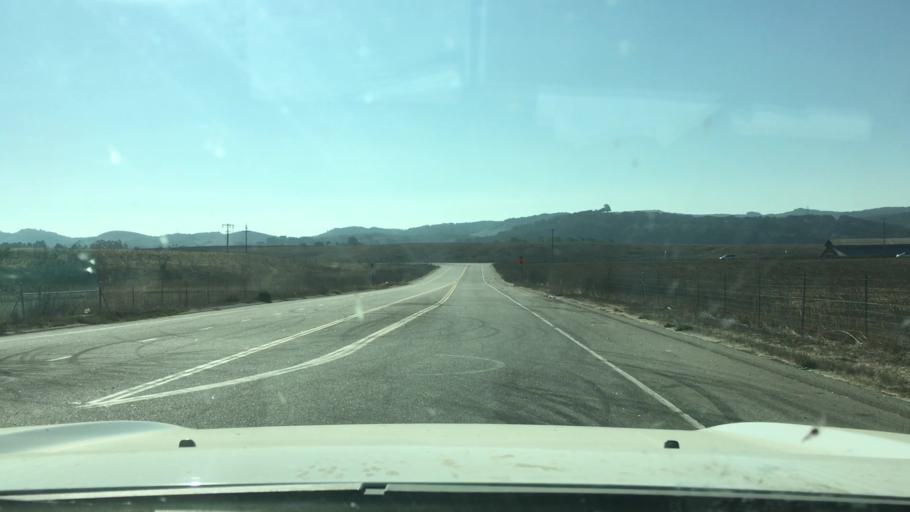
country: US
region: California
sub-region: San Luis Obispo County
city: San Luis Obispo
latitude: 35.2382
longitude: -120.6543
